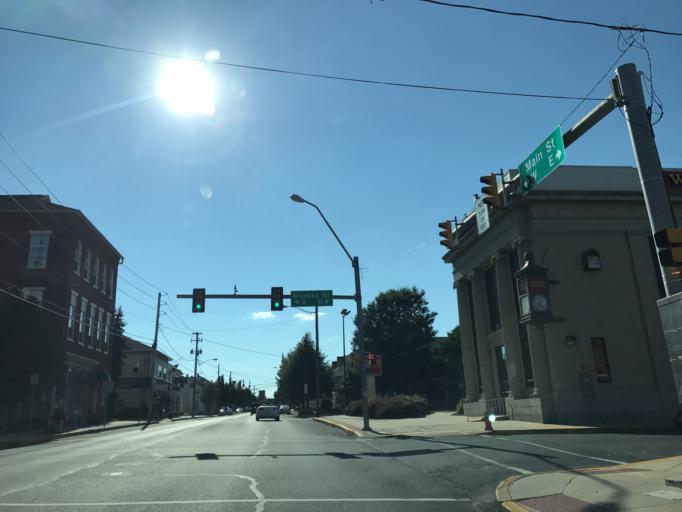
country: US
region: Pennsylvania
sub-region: Lancaster County
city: Mount Joy
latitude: 40.1099
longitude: -76.5030
